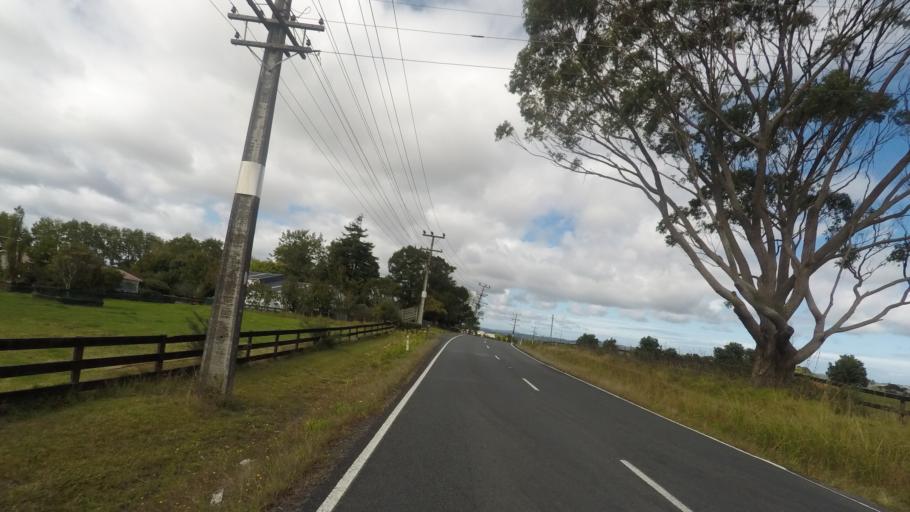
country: NZ
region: Auckland
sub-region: Auckland
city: Muriwai Beach
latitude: -36.7656
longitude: 174.5566
